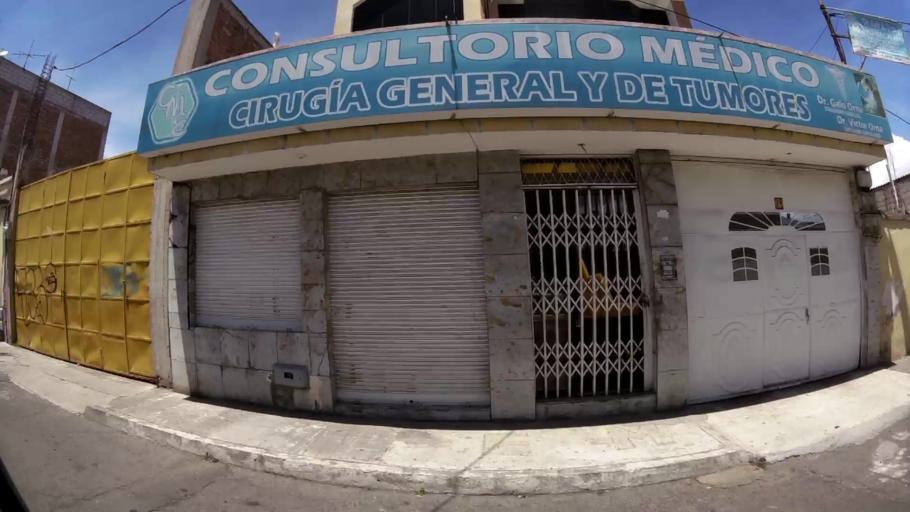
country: EC
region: Chimborazo
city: Riobamba
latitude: -1.6763
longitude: -78.6566
